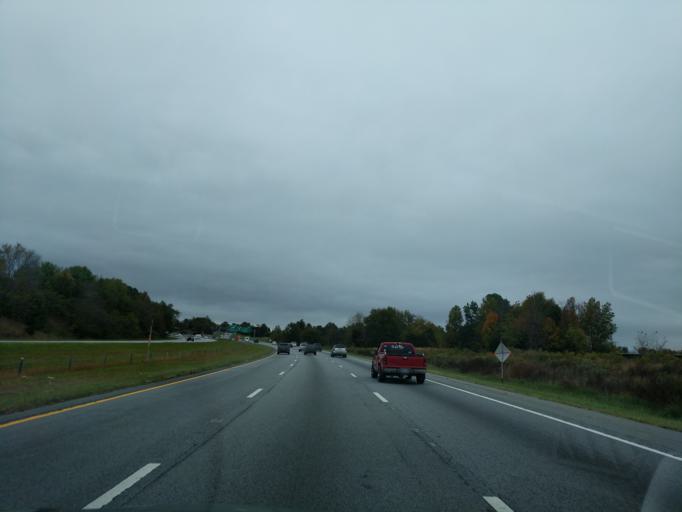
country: US
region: North Carolina
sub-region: Randolph County
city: Archdale
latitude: 35.8987
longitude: -79.9604
